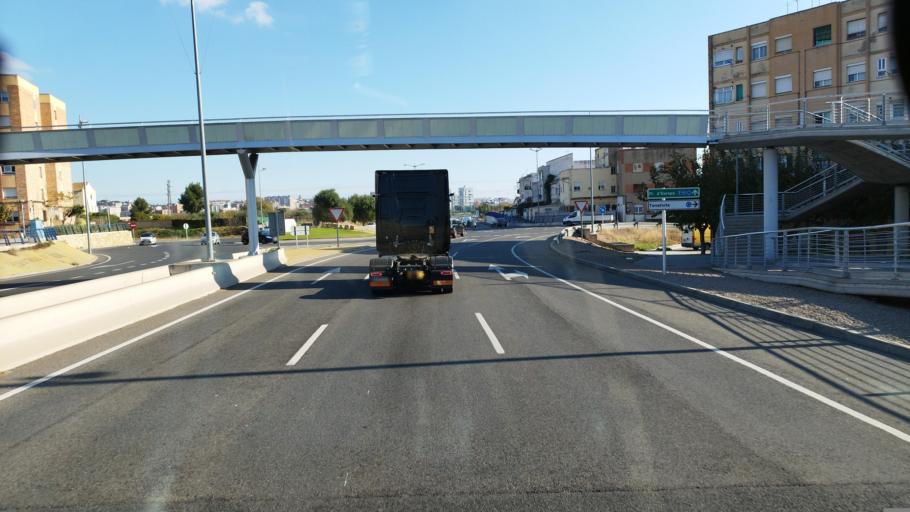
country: ES
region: Catalonia
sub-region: Provincia de Tarragona
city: Constanti
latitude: 41.1230
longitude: 1.2189
